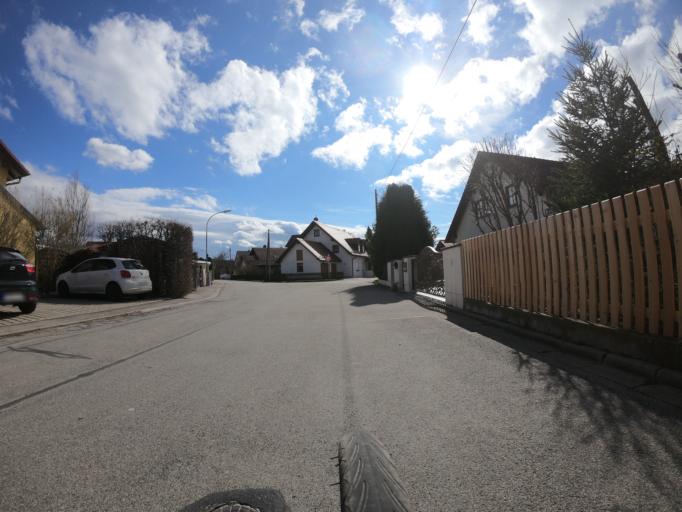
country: DE
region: Bavaria
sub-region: Upper Bavaria
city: Landsberied
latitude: 48.1784
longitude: 11.1927
